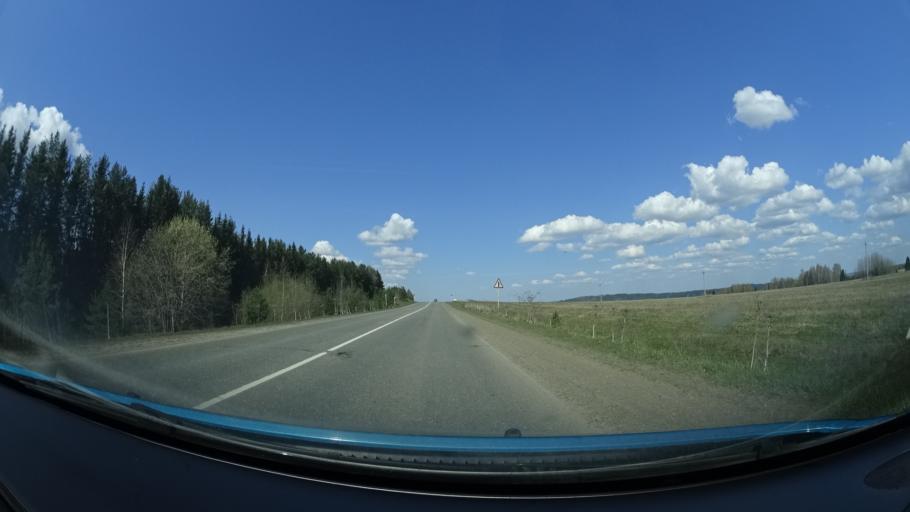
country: RU
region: Perm
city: Osa
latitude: 57.2657
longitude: 55.5737
